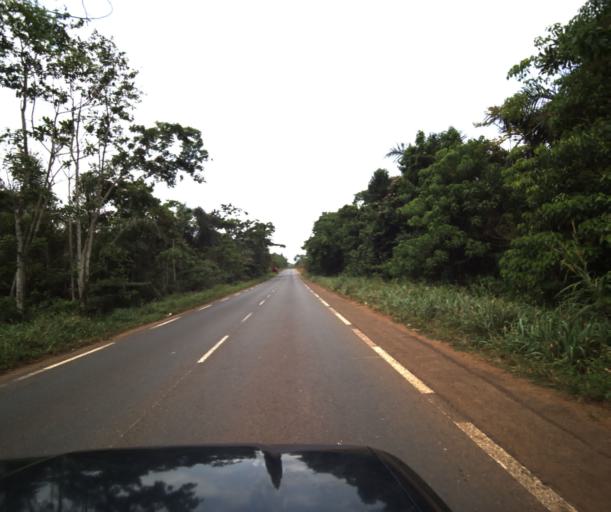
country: CM
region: Centre
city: Eseka
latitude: 3.8715
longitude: 10.9032
